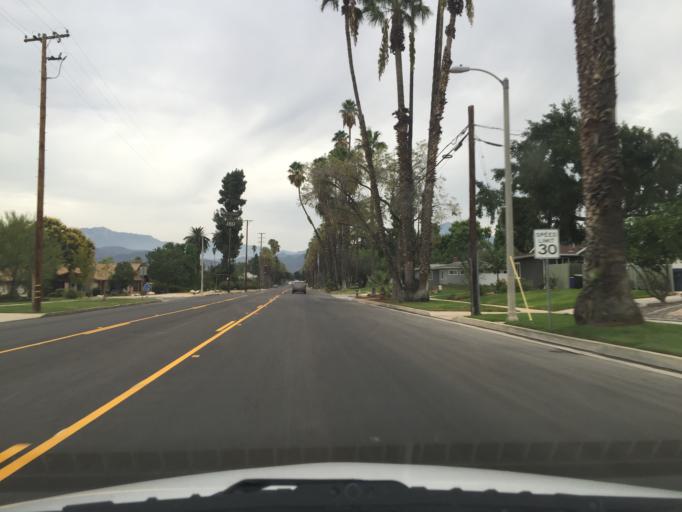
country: US
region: California
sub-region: San Bernardino County
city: Redlands
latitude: 34.0468
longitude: -117.1934
